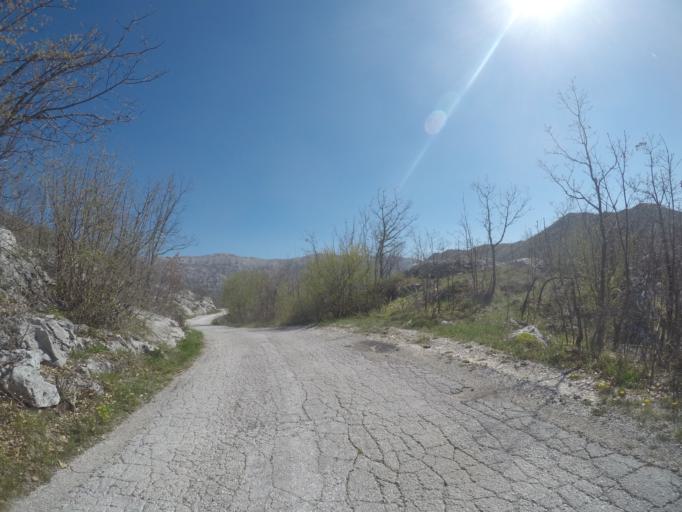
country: ME
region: Cetinje
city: Cetinje
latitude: 42.5346
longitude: 18.9781
